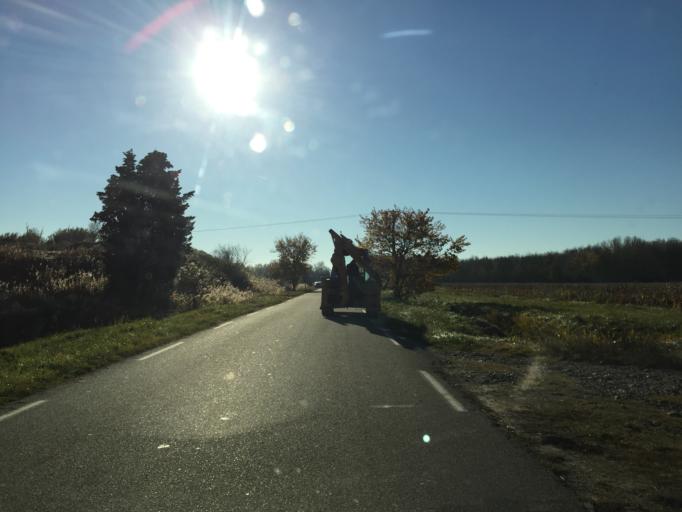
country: FR
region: Provence-Alpes-Cote d'Azur
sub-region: Departement du Vaucluse
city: Bedarrides
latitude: 44.0298
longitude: 4.9147
